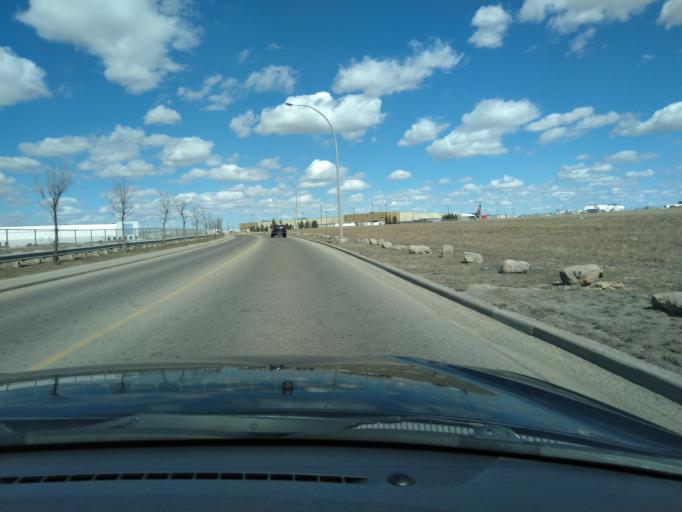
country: CA
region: Alberta
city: Calgary
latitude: 51.1146
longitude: -114.0295
